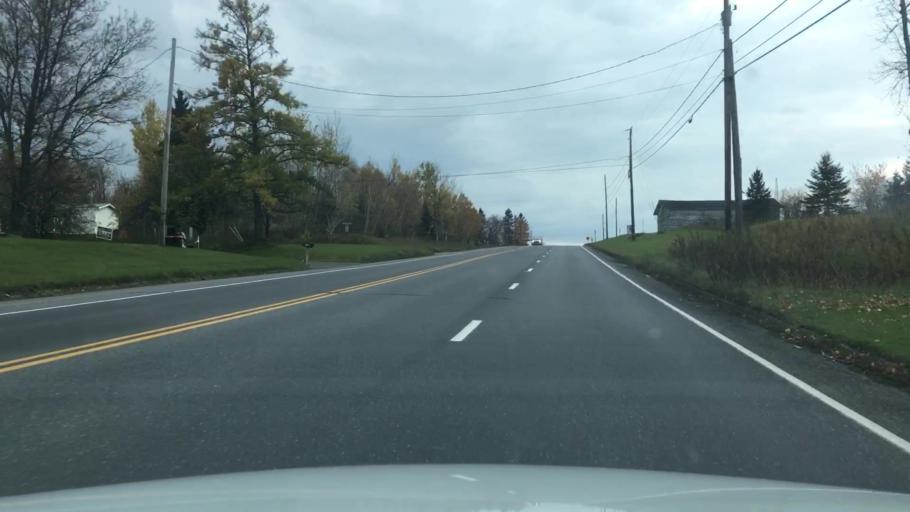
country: US
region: Maine
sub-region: Aroostook County
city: Caribou
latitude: 46.7823
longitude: -67.9890
